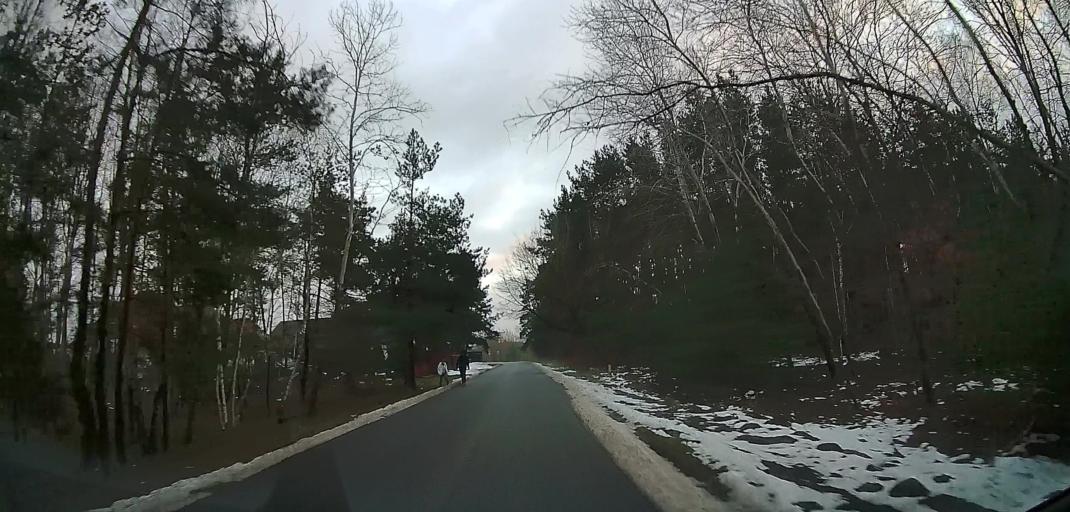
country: PL
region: Masovian Voivodeship
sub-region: Radom
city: Radom
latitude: 51.4517
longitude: 21.1311
